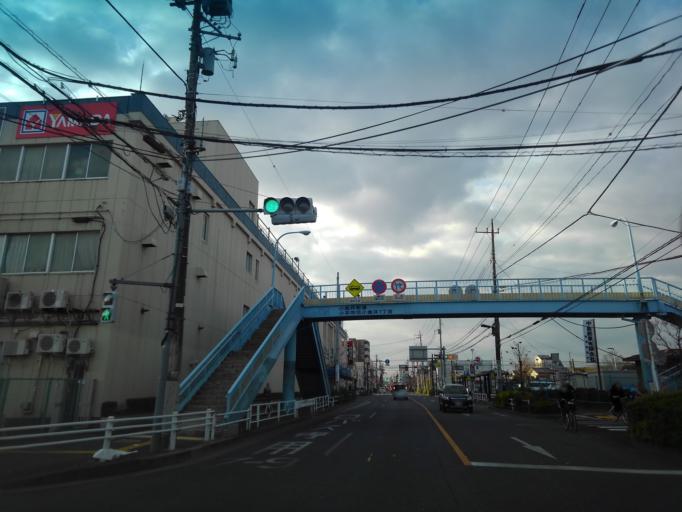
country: JP
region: Tokyo
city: Tanashicho
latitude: 35.7284
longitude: 139.5116
